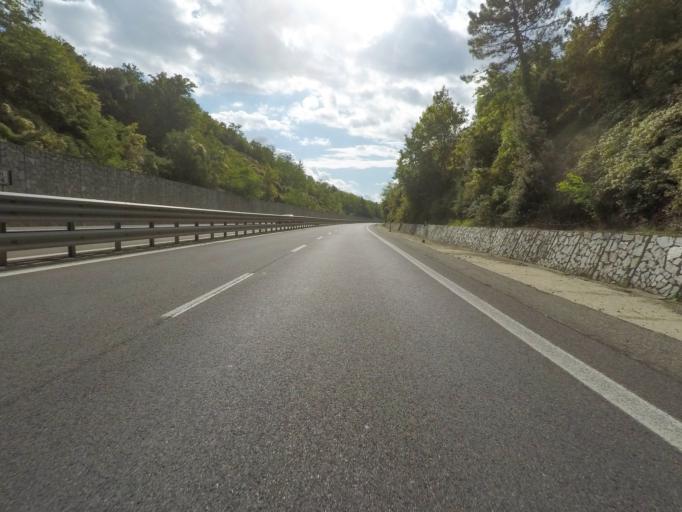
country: IT
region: Tuscany
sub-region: Provincia di Siena
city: Serre di Rapolano
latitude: 43.2819
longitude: 11.6280
